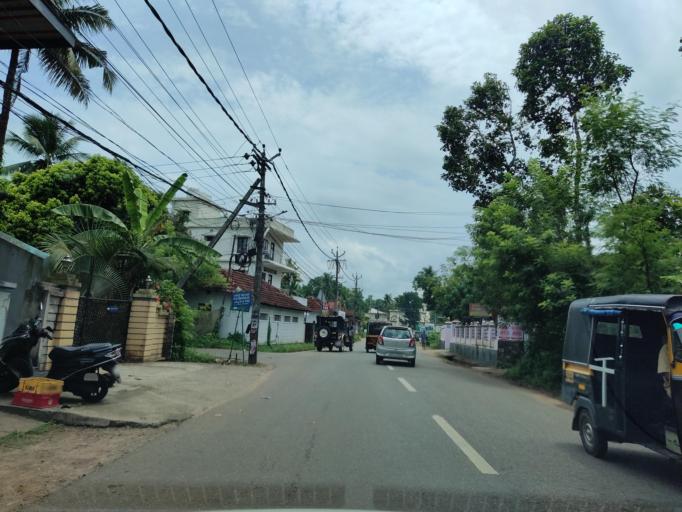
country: IN
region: Kerala
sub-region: Pattanamtitta
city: Adur
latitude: 9.2297
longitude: 76.6630
